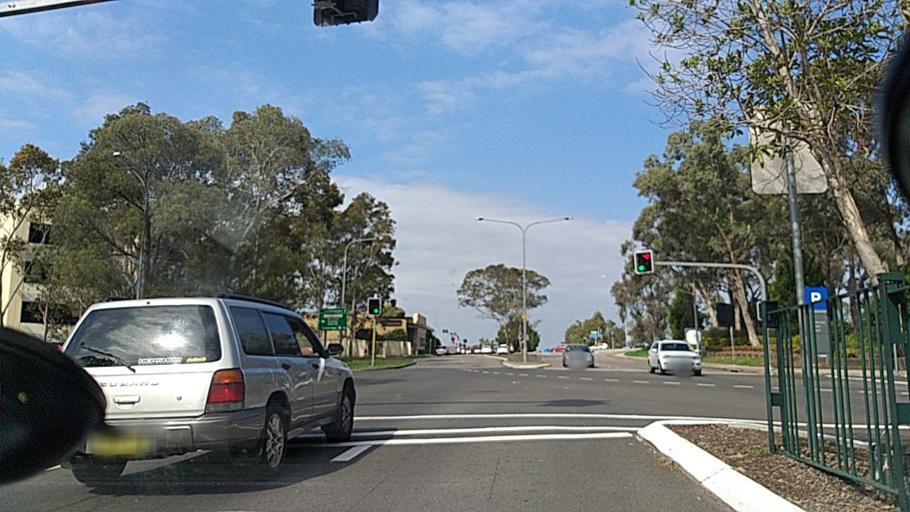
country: AU
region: New South Wales
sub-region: Campbelltown Municipality
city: Glen Alpine
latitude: -34.0739
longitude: 150.7987
